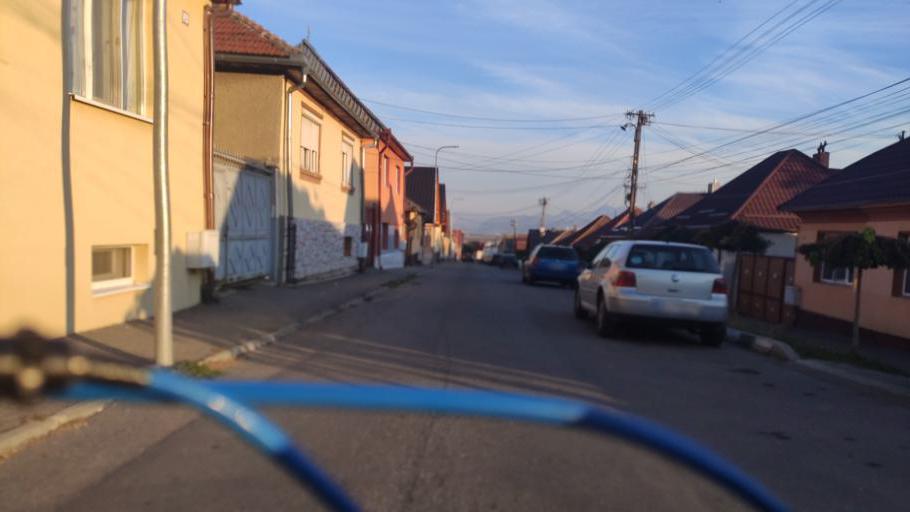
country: RO
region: Brasov
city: Codlea
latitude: 45.7069
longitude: 25.4472
